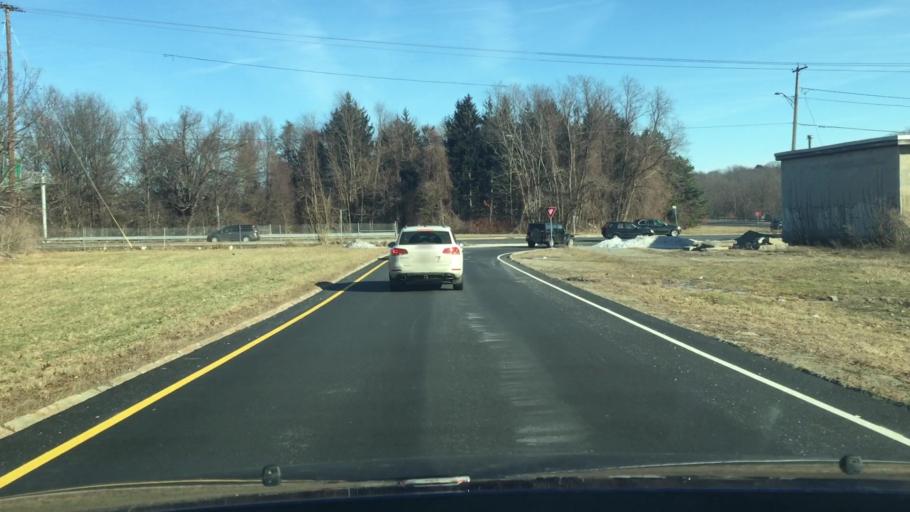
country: US
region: Massachusetts
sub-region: Essex County
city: North Andover
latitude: 42.6852
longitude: -71.1425
